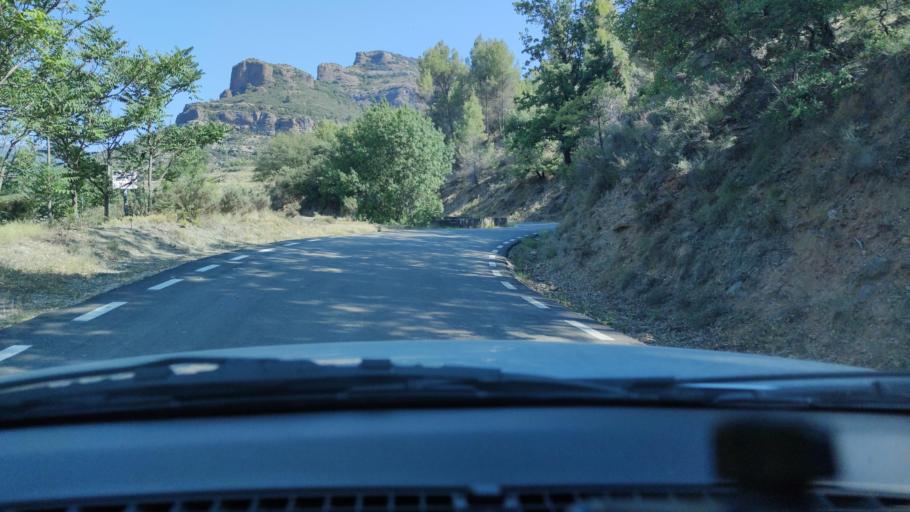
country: ES
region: Catalonia
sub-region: Provincia de Lleida
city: Senterada
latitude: 42.2715
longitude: 0.9519
